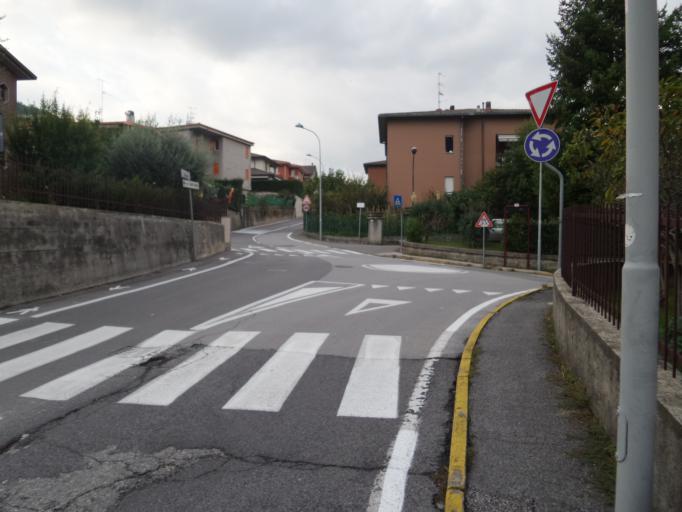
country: IT
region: Lombardy
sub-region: Provincia di Lecco
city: Olginate
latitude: 45.7952
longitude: 9.4113
